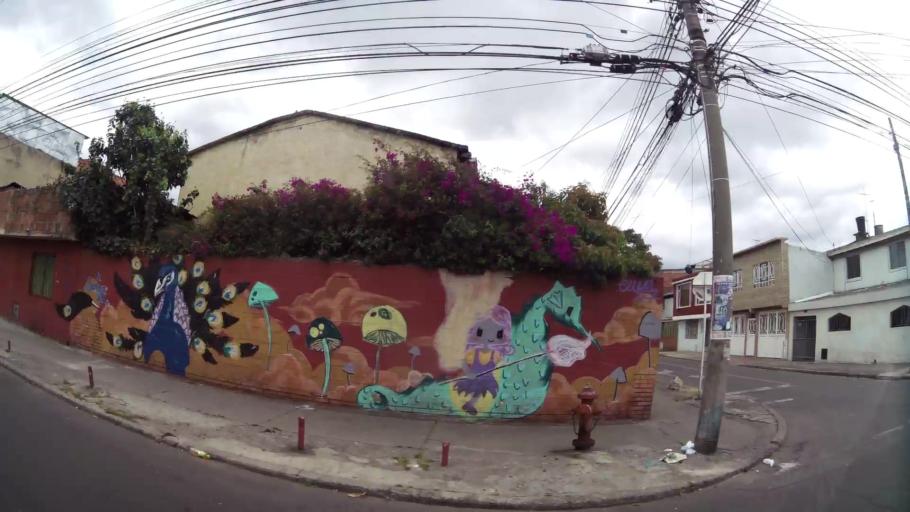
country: CO
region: Bogota D.C.
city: Bogota
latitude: 4.6157
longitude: -74.1195
